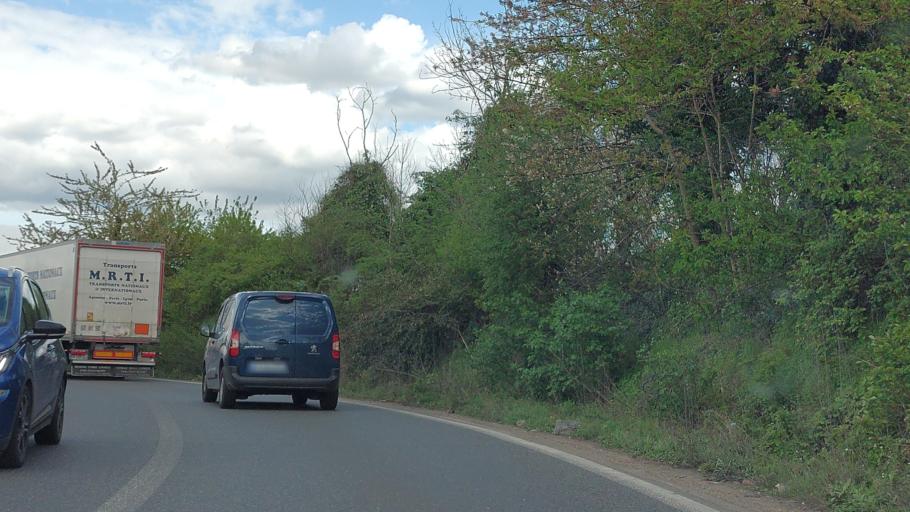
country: FR
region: Ile-de-France
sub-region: Departement du Val-d'Oise
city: Saint-Ouen-l'Aumone
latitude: 49.0490
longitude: 2.1485
